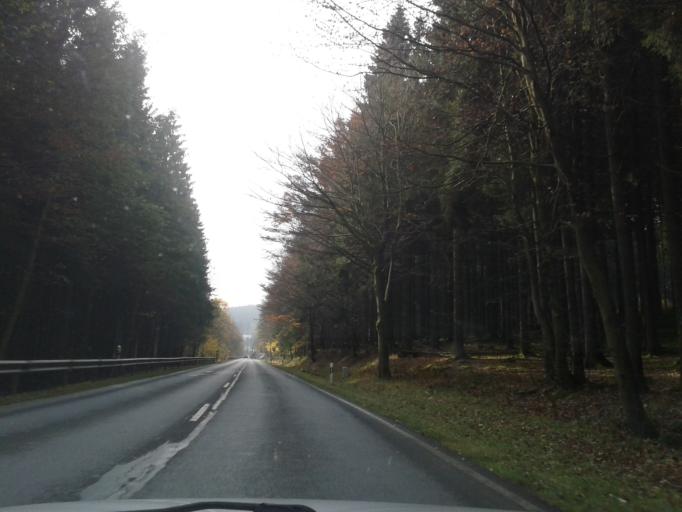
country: DE
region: North Rhine-Westphalia
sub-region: Regierungsbezirk Arnsberg
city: Winterberg
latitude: 51.1727
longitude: 8.4909
